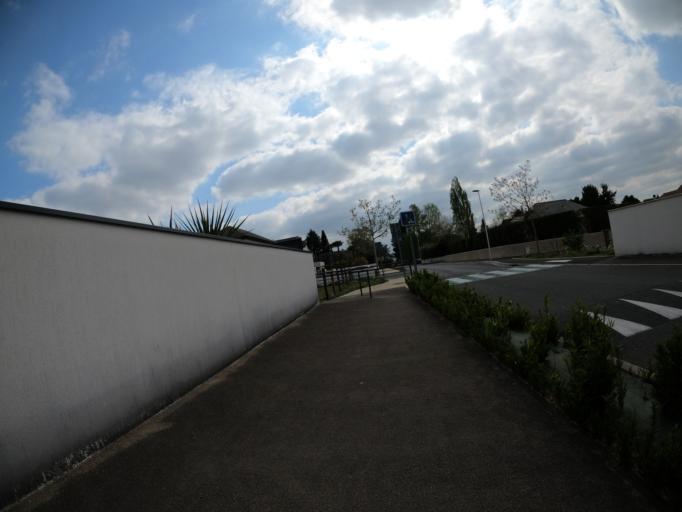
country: FR
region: Aquitaine
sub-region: Departement des Pyrenees-Atlantiques
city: Lons
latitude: 43.3394
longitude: -0.3913
